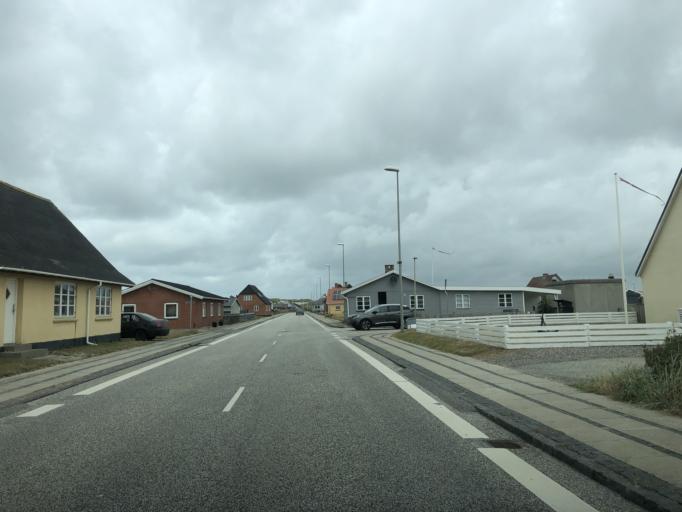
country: DK
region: Central Jutland
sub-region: Holstebro Kommune
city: Ulfborg
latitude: 56.3744
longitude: 8.1209
